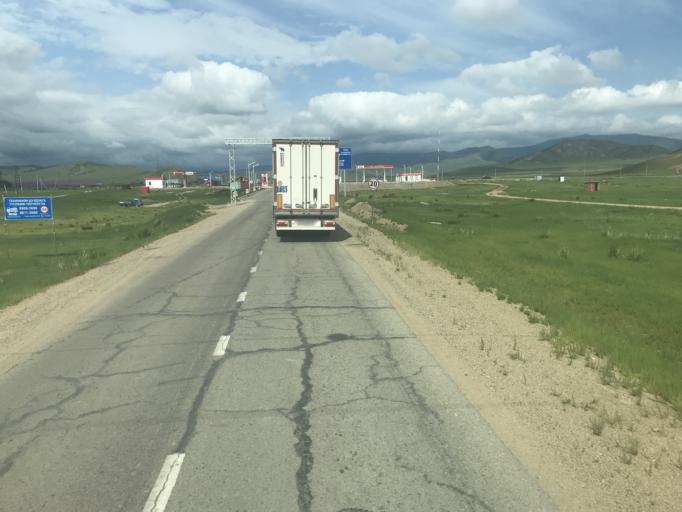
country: MN
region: Darhan Uul
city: Orhon
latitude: 49.8968
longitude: 106.2599
